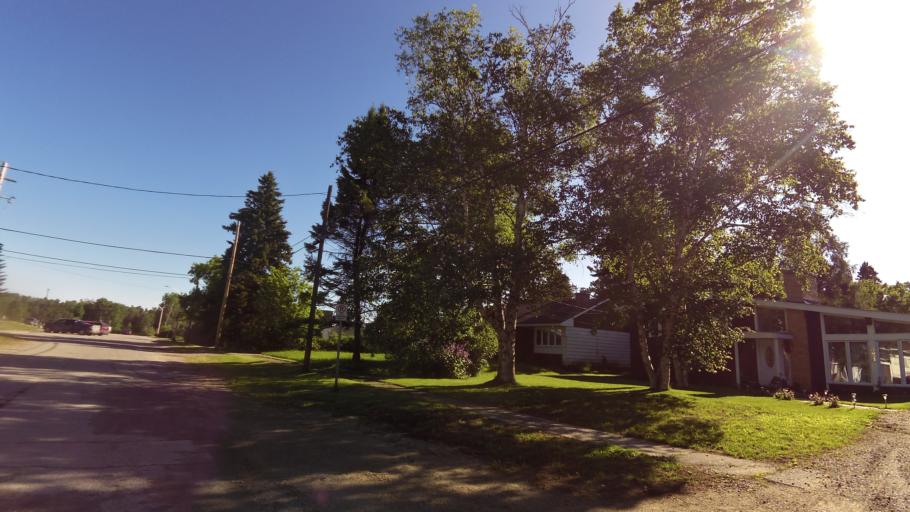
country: CA
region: Ontario
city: Iroquois Falls
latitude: 48.5384
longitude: -80.4697
